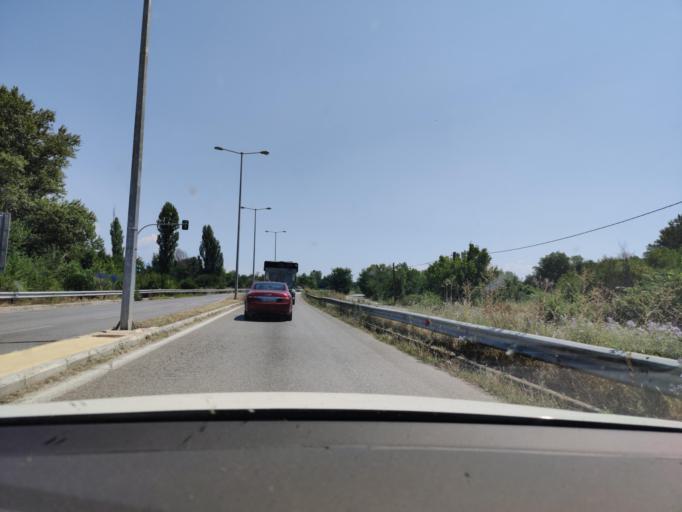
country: GR
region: Central Macedonia
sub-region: Nomos Serron
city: Serres
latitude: 41.0757
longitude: 23.5410
